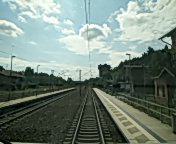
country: DE
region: Brandenburg
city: Halbe
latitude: 52.0300
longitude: 13.7215
